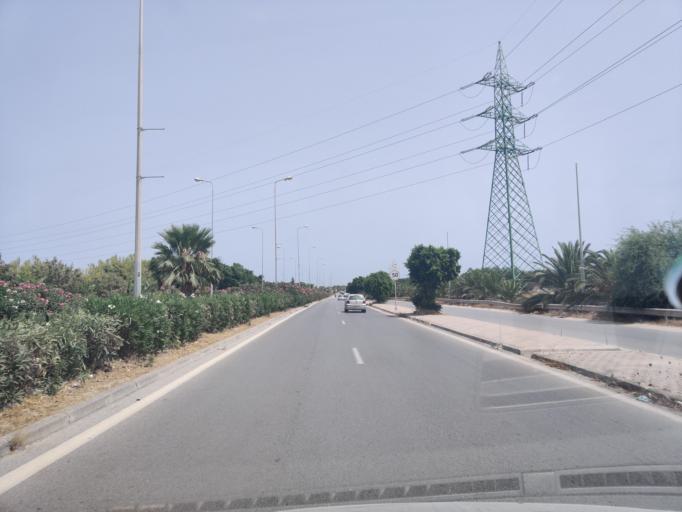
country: TN
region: Tunis
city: Carthage
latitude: 36.8546
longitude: 10.3092
